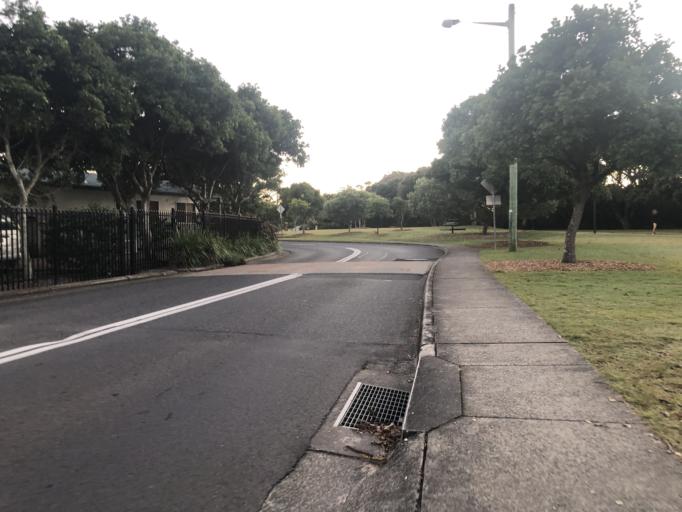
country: AU
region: New South Wales
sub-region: Coffs Harbour
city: Coffs Harbour
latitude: -30.2941
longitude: 153.1382
